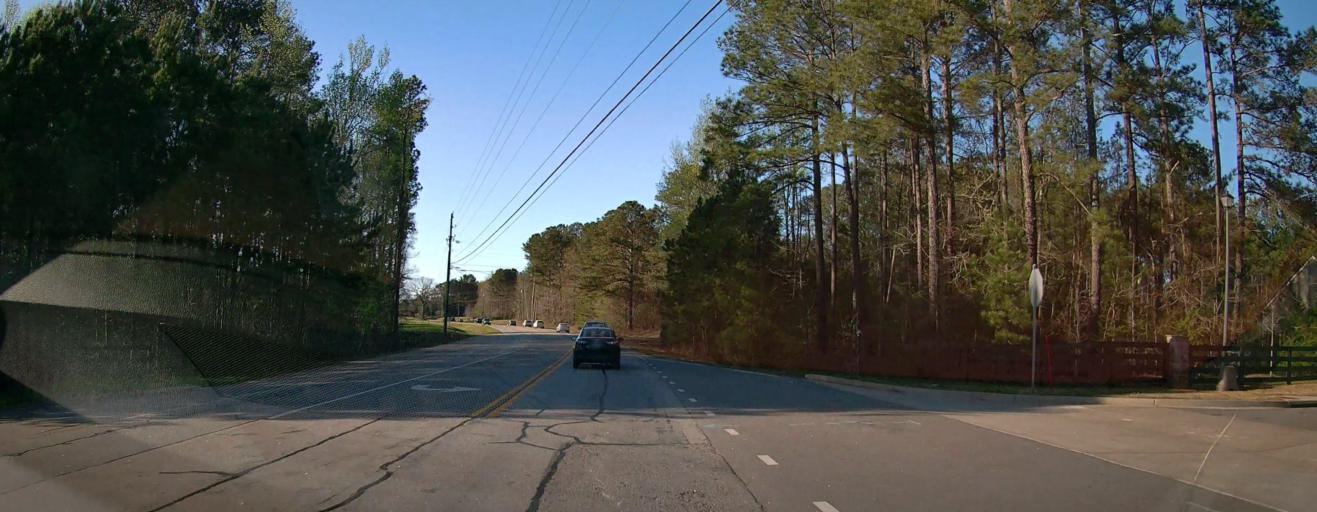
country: US
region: Georgia
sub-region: Newton County
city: Oakwood
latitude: 33.4557
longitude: -83.9035
